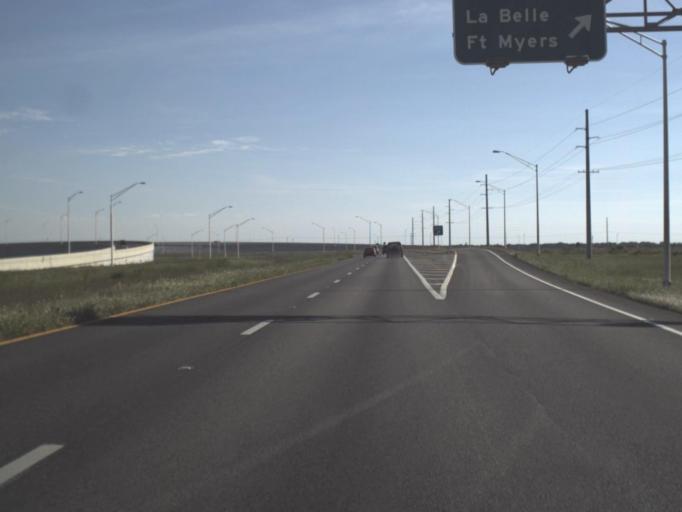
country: US
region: Florida
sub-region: Glades County
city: Moore Haven
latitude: 26.7603
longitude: -81.0832
